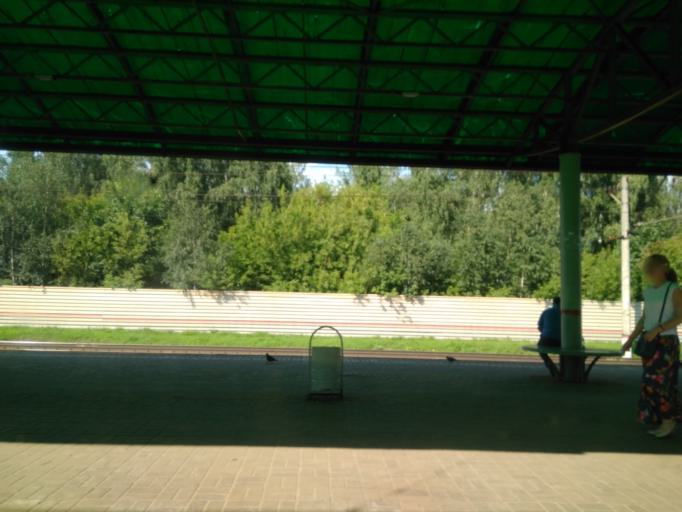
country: RU
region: Moskovskaya
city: Tomilino
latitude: 55.6554
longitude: 37.9540
